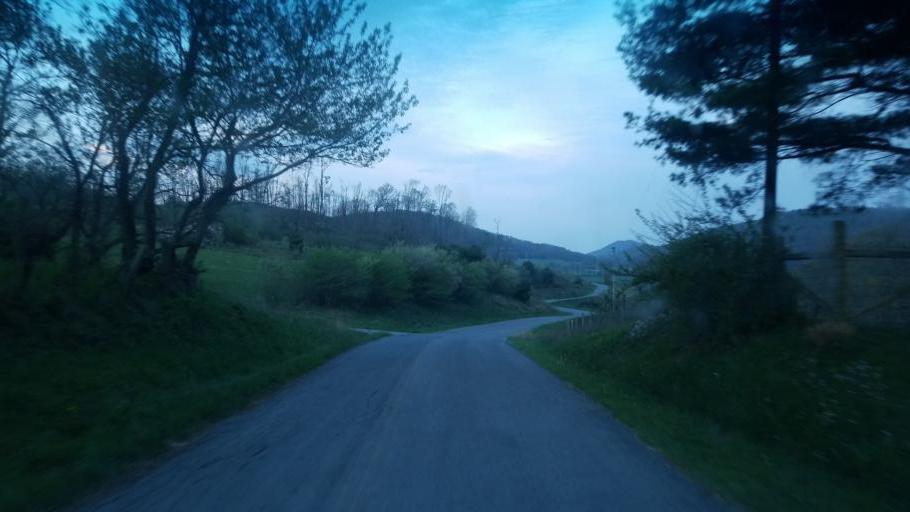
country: US
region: Virginia
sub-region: Smyth County
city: Marion
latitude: 36.7621
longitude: -81.4614
